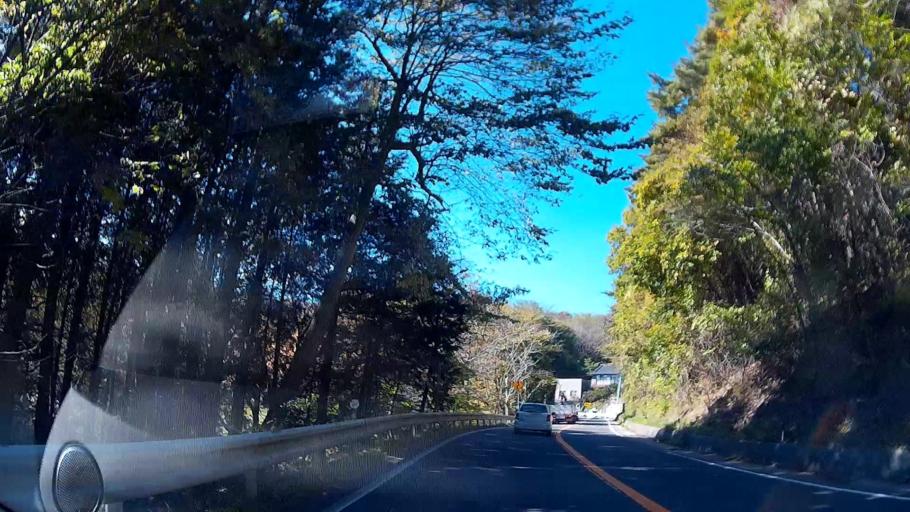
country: JP
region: Nagano
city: Okaya
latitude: 36.0777
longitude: 138.0365
